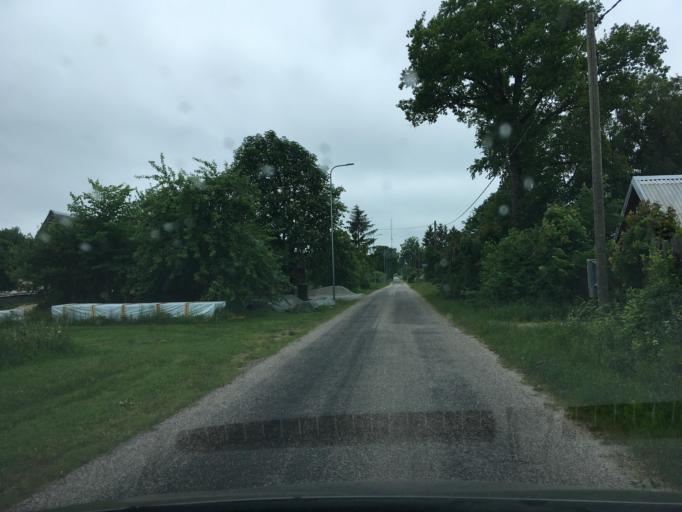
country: EE
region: Laeaene
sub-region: Lihula vald
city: Lihula
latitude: 58.6799
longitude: 23.8365
